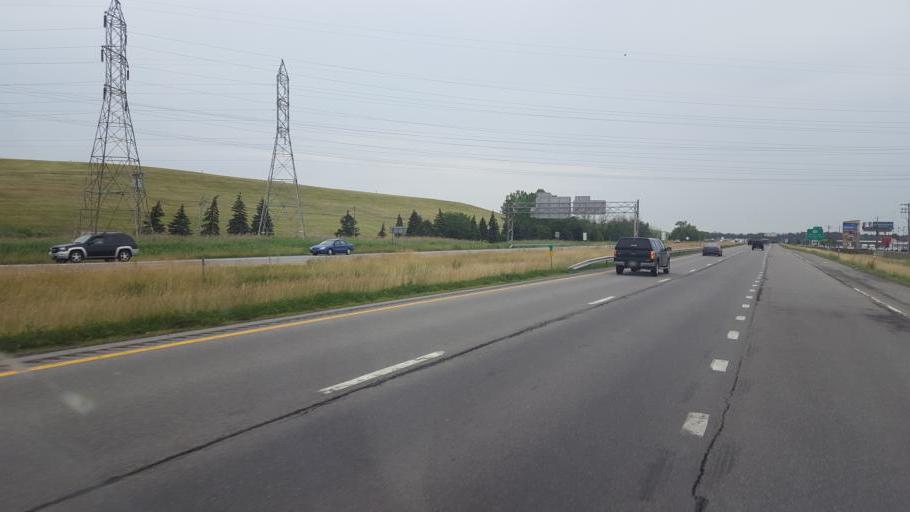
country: US
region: New York
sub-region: Niagara County
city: Niagara Falls
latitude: 43.0921
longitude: -78.9885
